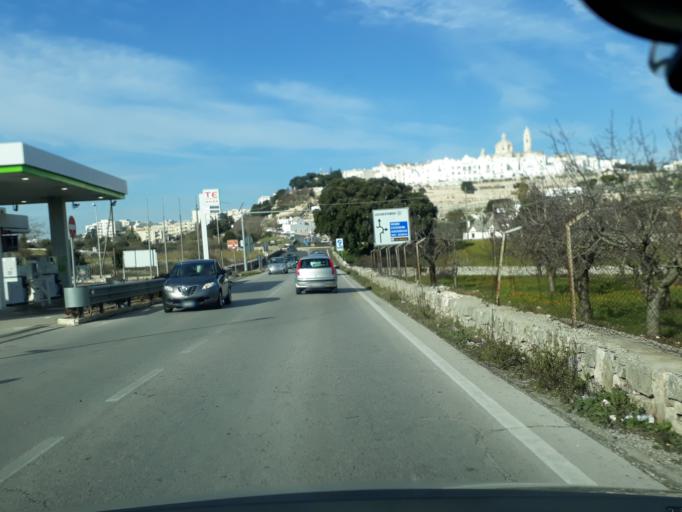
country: IT
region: Apulia
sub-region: Provincia di Bari
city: Locorotondo
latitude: 40.7475
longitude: 17.3302
